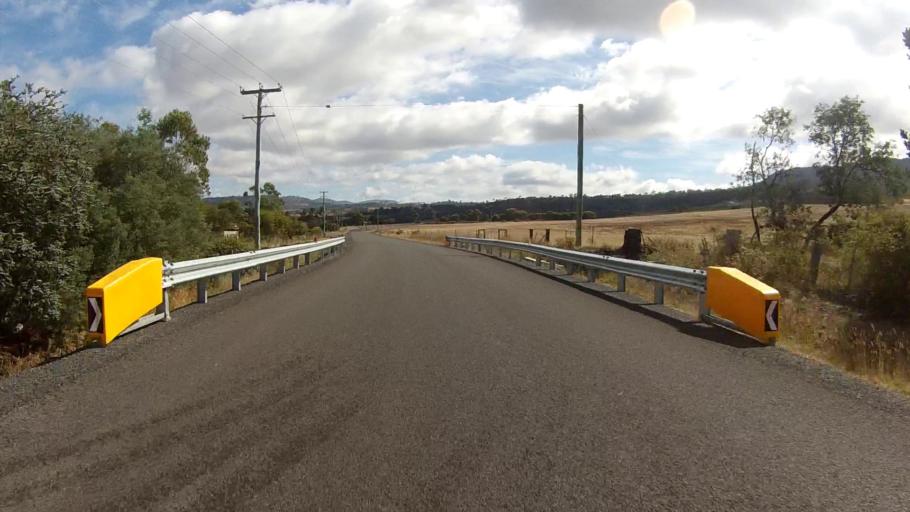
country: AU
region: Tasmania
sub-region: Brighton
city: Old Beach
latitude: -42.7631
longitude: 147.3005
